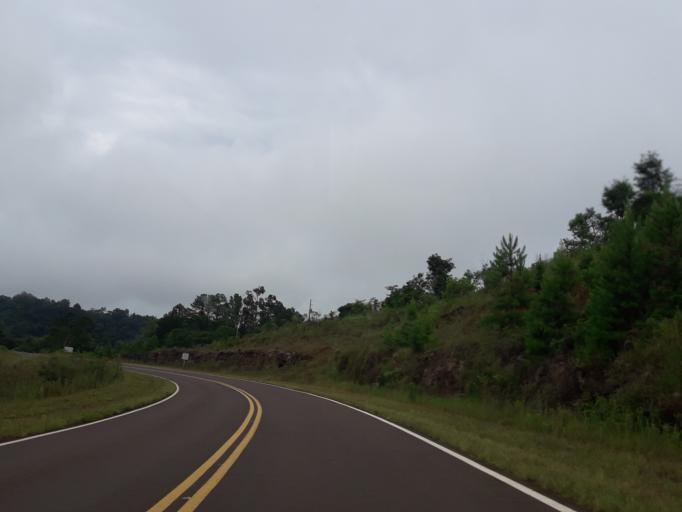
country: AR
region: Misiones
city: Bernardo de Irigoyen
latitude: -26.3959
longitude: -53.8146
